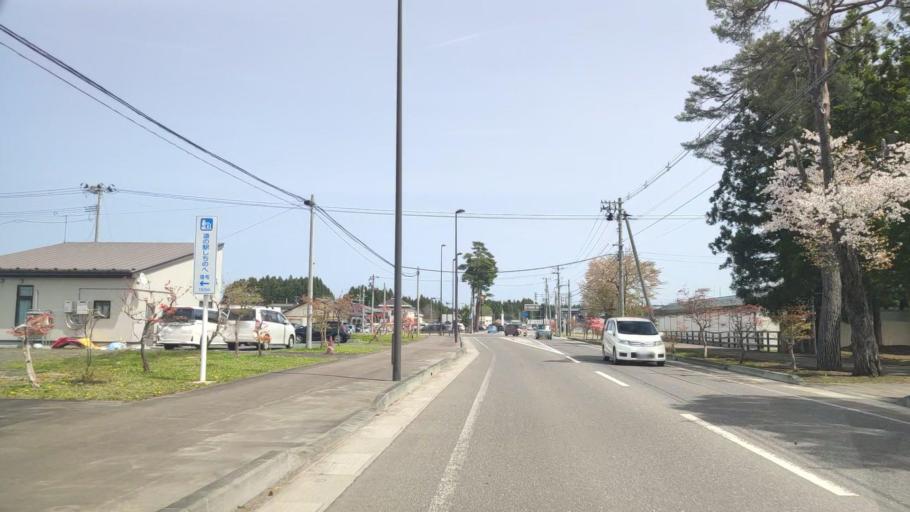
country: JP
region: Aomori
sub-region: Misawa Shi
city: Inuotose
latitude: 40.7161
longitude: 141.1531
